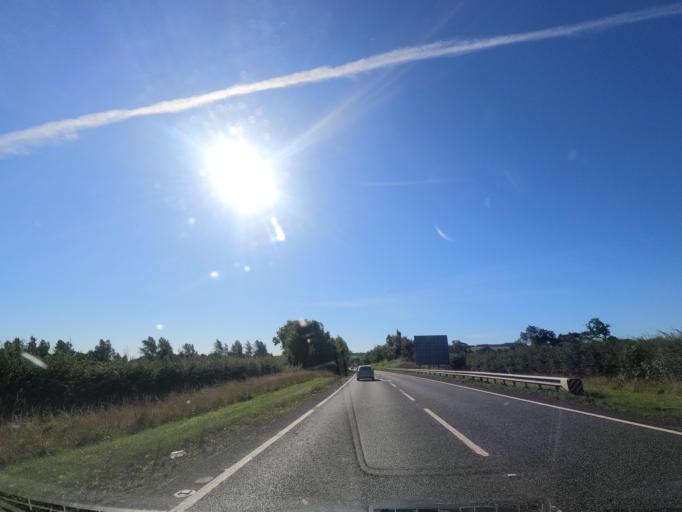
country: GB
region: England
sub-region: Northumberland
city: Belford
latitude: 55.5939
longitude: -1.8140
